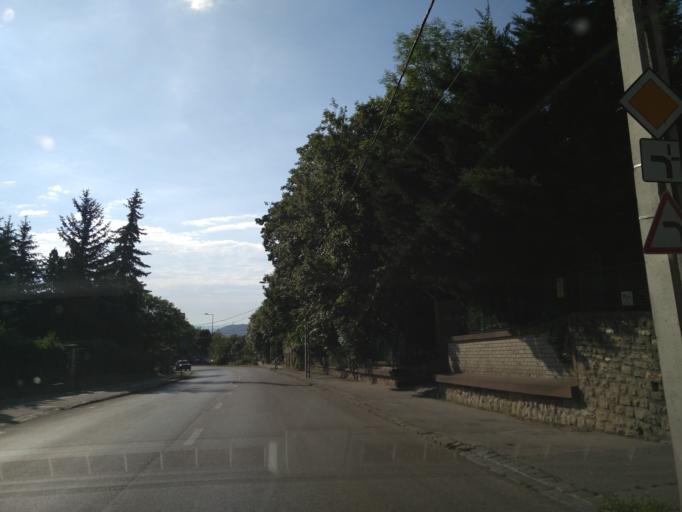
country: HU
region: Budapest
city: Budapest XII. keruelet
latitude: 47.5033
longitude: 19.0002
